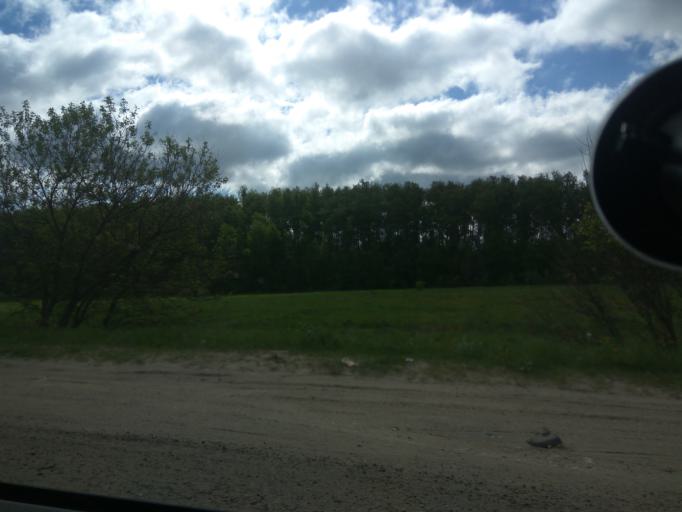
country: RU
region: Moskovskaya
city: Ostrovtsy
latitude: 55.5453
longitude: 38.0657
